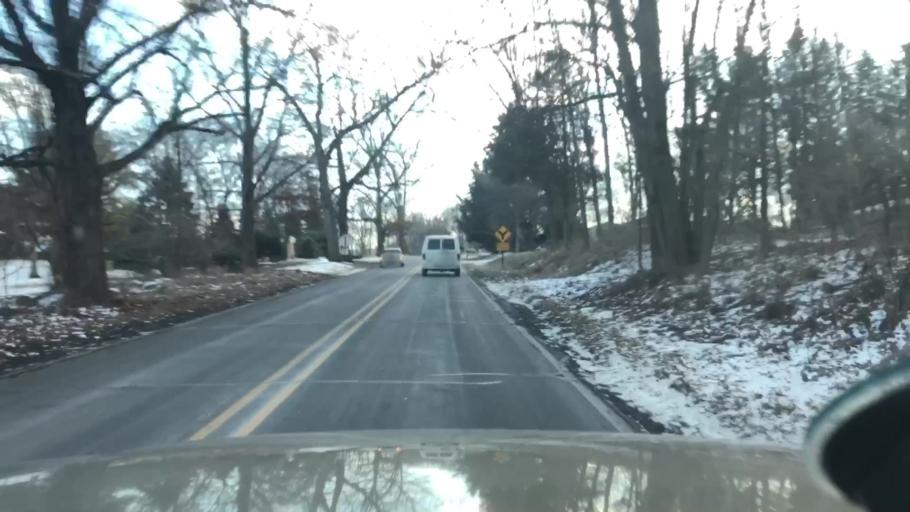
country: US
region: Michigan
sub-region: Jackson County
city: Vandercook Lake
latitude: 42.1843
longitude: -84.4570
